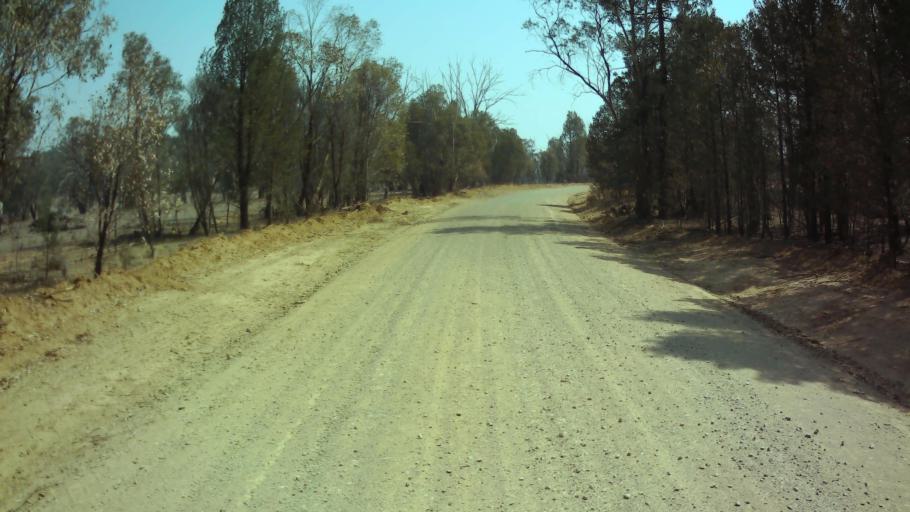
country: AU
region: New South Wales
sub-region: Weddin
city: Grenfell
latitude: -33.6646
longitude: 148.2742
